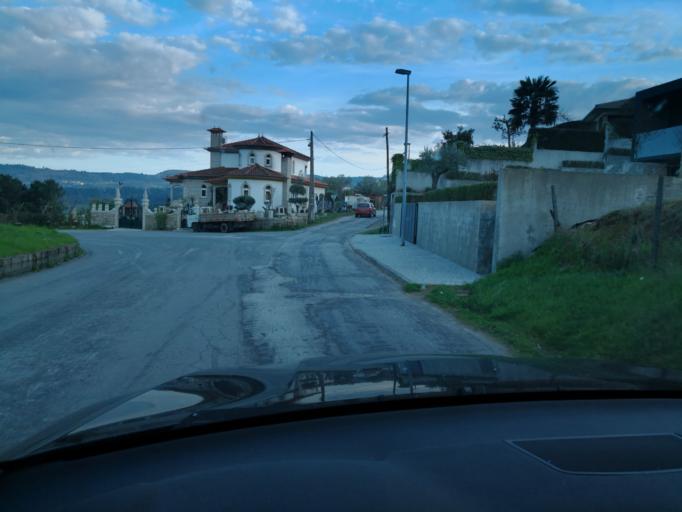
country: PT
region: Vila Real
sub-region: Vila Real
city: Vila Real
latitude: 41.3013
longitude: -7.7779
